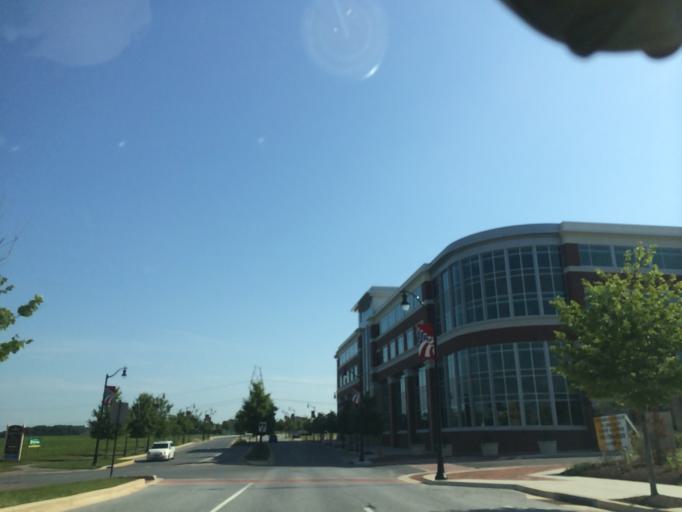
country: US
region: Maryland
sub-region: Howard County
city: Fulton
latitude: 39.1502
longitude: -76.9039
